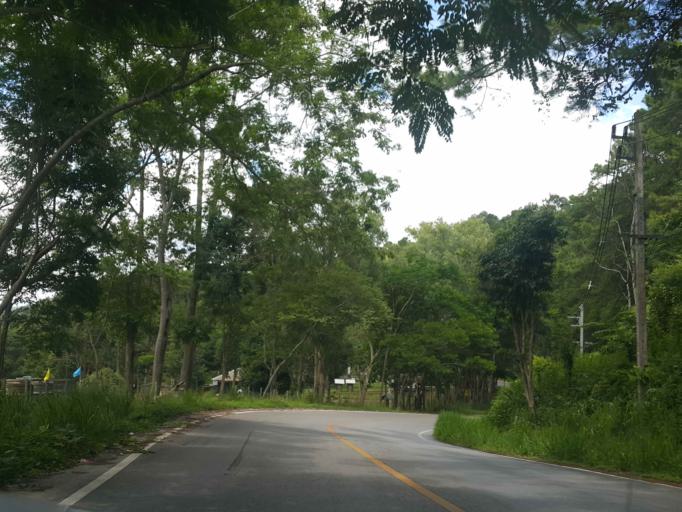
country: TH
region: Chiang Mai
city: Samoeng
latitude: 18.8764
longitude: 98.7932
